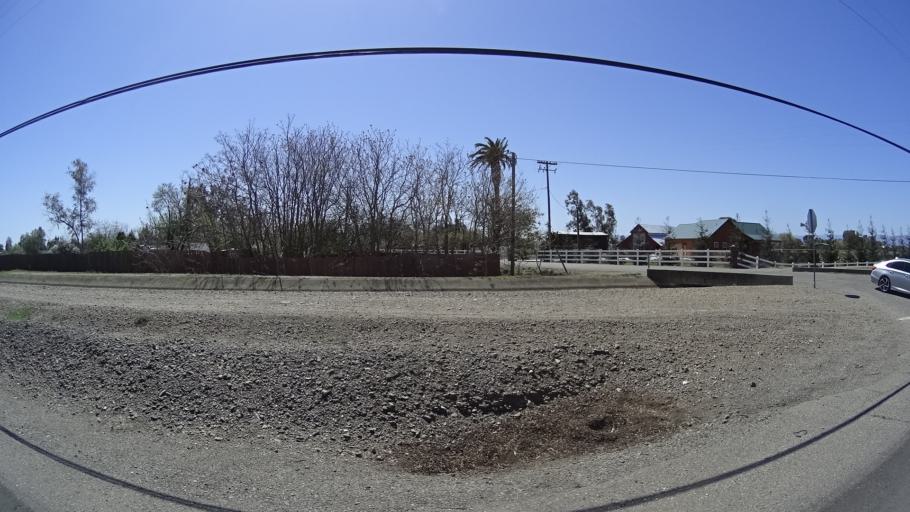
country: US
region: California
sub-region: Glenn County
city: Orland
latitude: 39.7604
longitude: -122.2297
